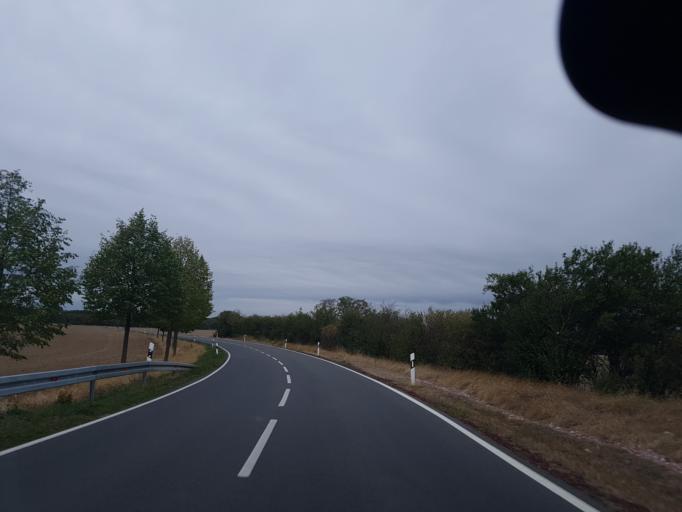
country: DE
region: Saxony-Anhalt
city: Prettin
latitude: 51.6508
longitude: 12.9740
